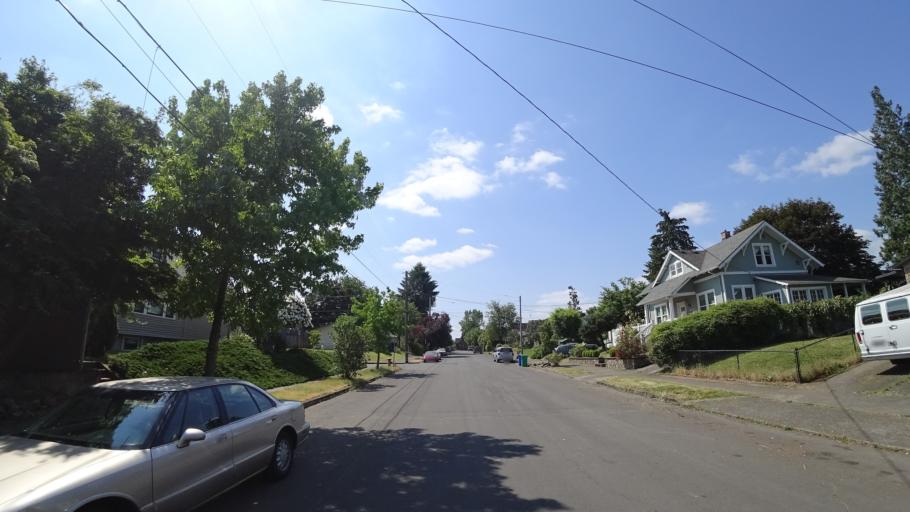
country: US
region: Oregon
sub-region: Multnomah County
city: Portland
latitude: 45.5699
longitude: -122.6562
